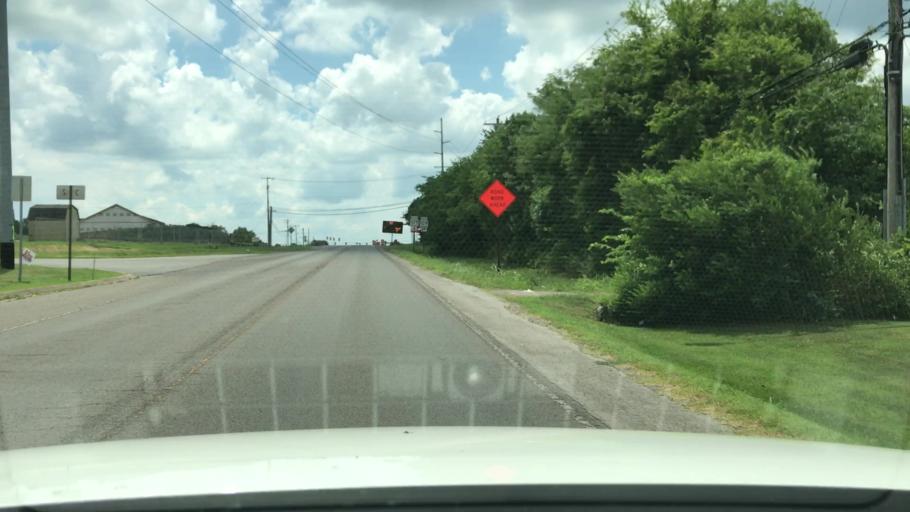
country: US
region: Tennessee
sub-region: Sumner County
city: Gallatin
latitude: 36.3671
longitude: -86.4405
